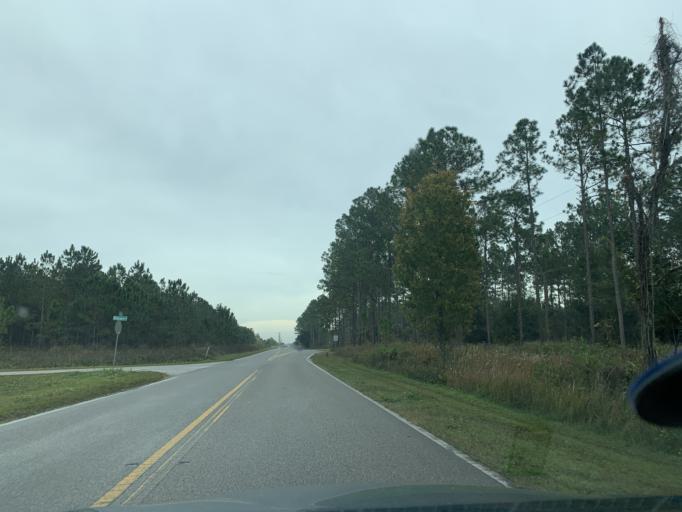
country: US
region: Florida
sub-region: Pasco County
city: Wesley Chapel
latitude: 28.2735
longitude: -82.3250
